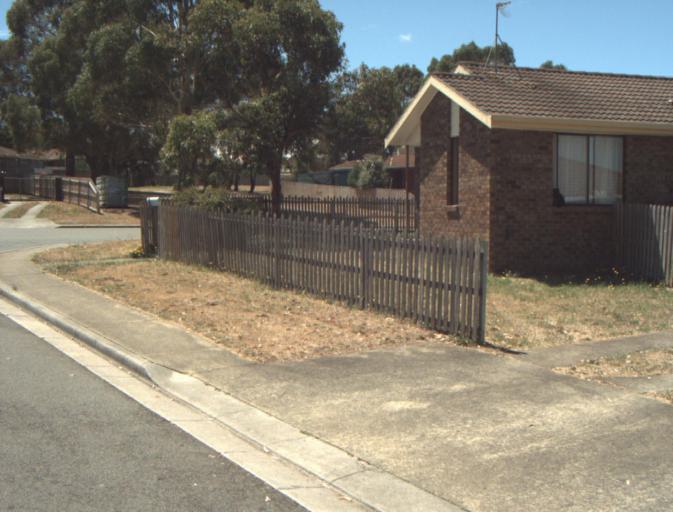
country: AU
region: Tasmania
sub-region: Launceston
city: Mayfield
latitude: -41.3803
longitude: 147.1331
